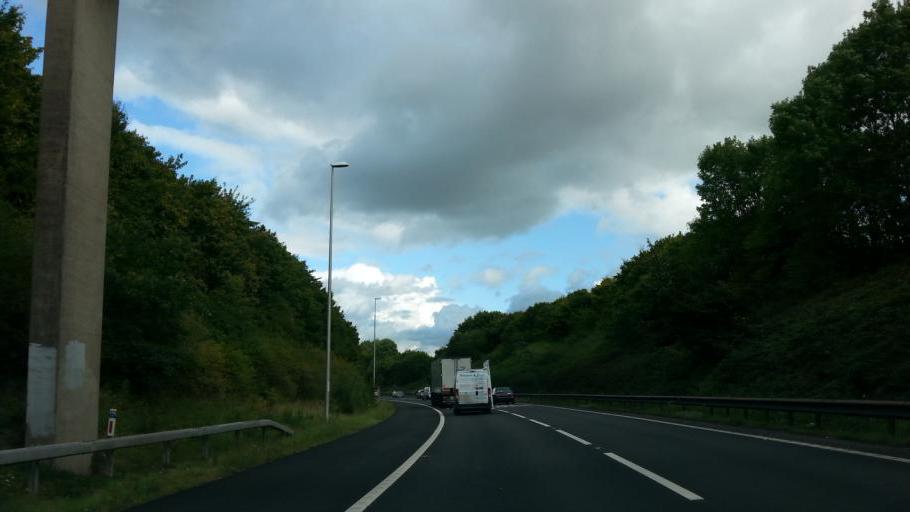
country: GB
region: England
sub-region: Warwickshire
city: Water Orton
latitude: 52.5073
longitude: -1.7416
